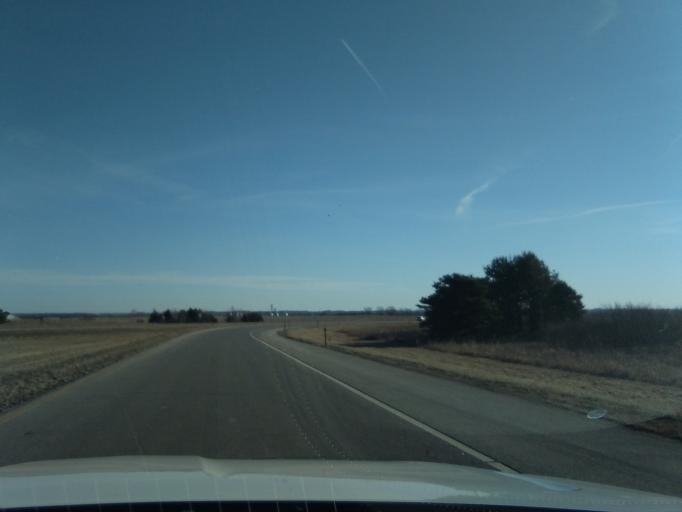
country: US
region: Nebraska
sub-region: Seward County
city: Milford
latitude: 40.8213
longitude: -97.0998
